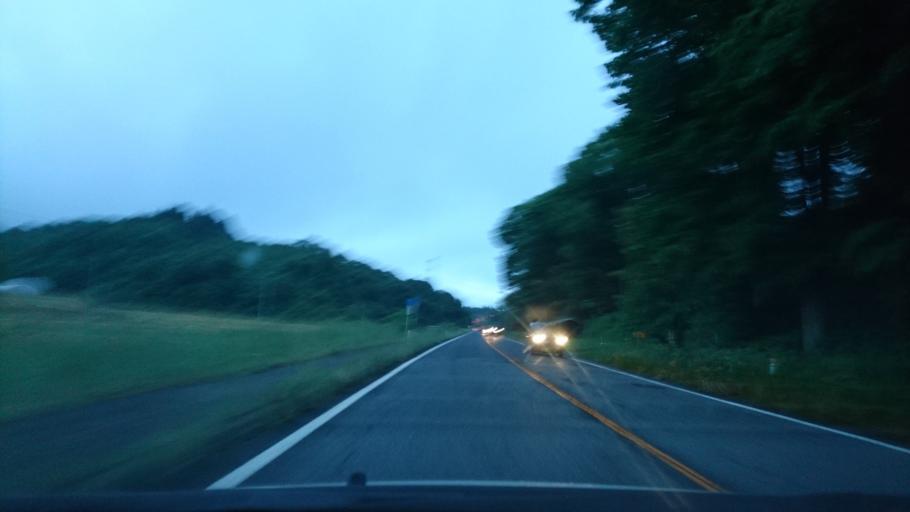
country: JP
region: Iwate
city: Ichinoseki
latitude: 38.8628
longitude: 141.1058
